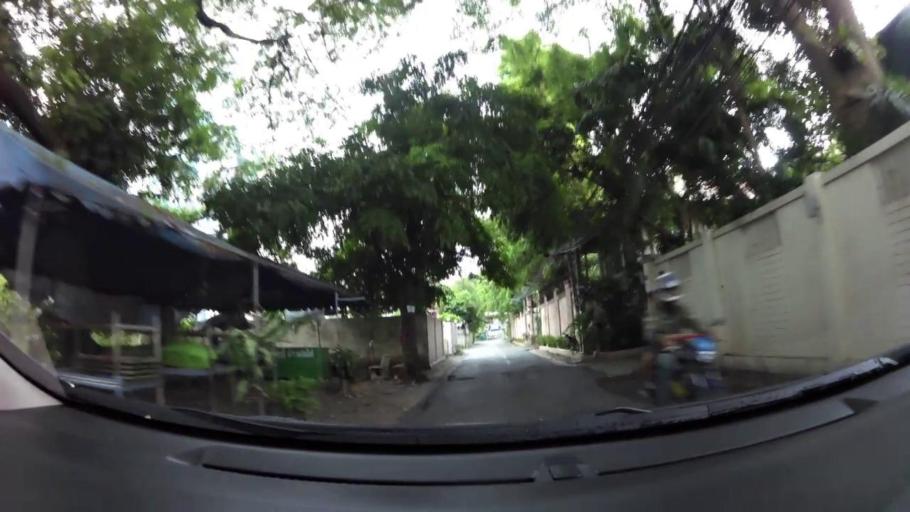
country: TH
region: Bangkok
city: Phra Khanong
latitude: 13.7056
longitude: 100.6150
